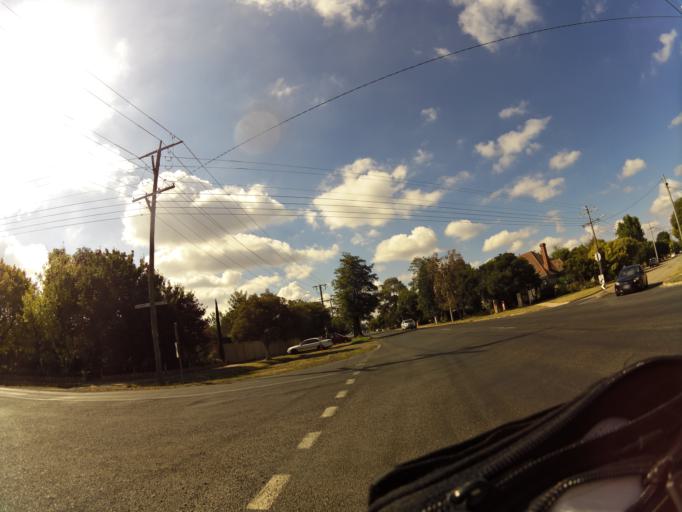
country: AU
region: Victoria
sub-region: Benalla
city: Benalla
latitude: -36.5542
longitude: 145.9911
